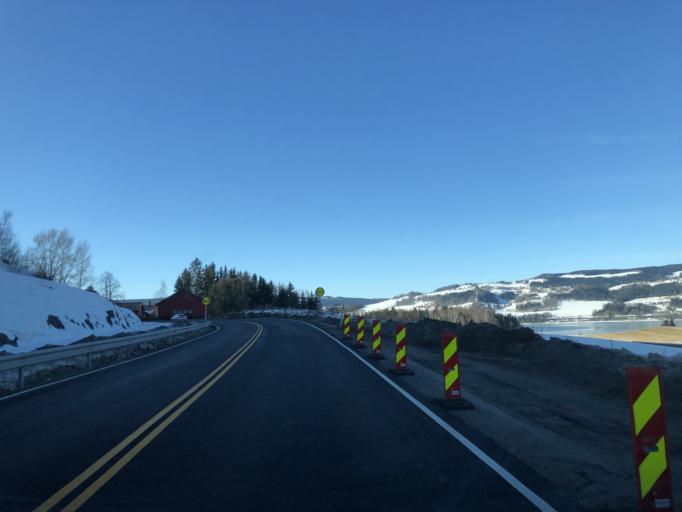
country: NO
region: Hedmark
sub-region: Ringsaker
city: Moelv
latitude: 60.9109
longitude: 10.7068
